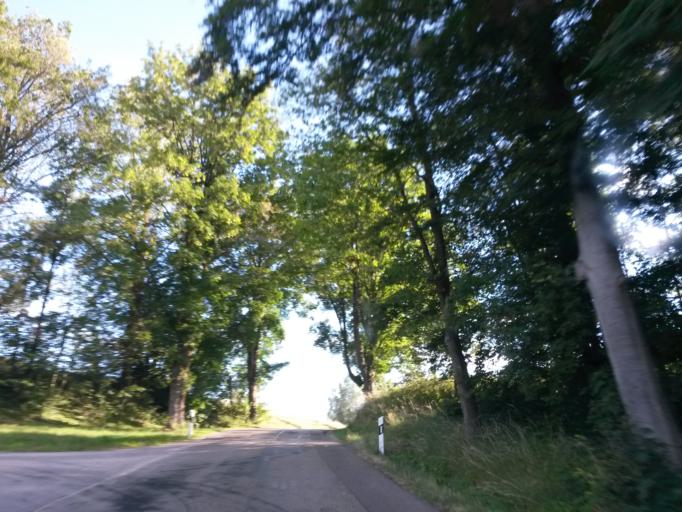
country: DE
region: Baden-Wuerttemberg
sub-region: Regierungsbezirk Stuttgart
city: Ellenberg
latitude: 49.0766
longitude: 10.2093
